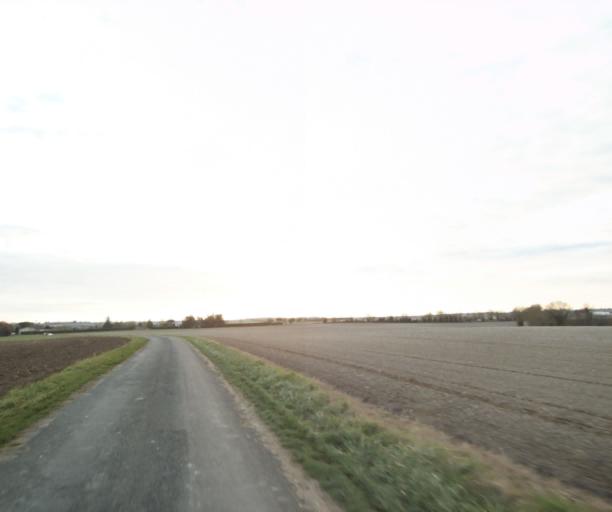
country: FR
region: Poitou-Charentes
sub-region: Departement de la Charente-Maritime
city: Les Gonds
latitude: 45.7020
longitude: -0.6166
